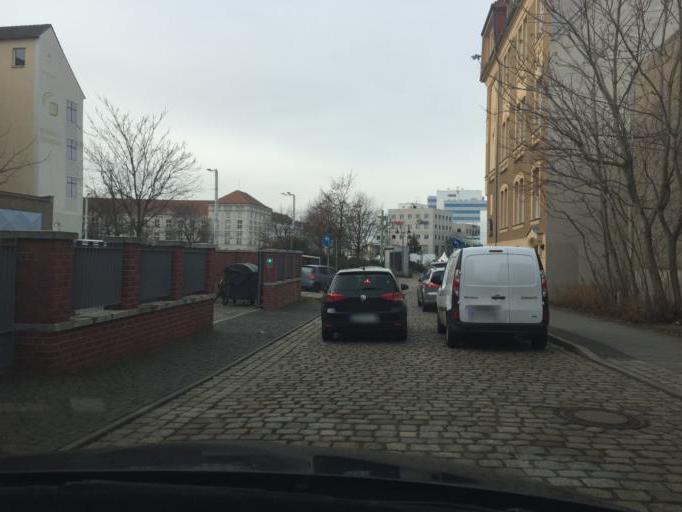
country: DE
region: Brandenburg
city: Cottbus
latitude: 51.7615
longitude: 14.3323
